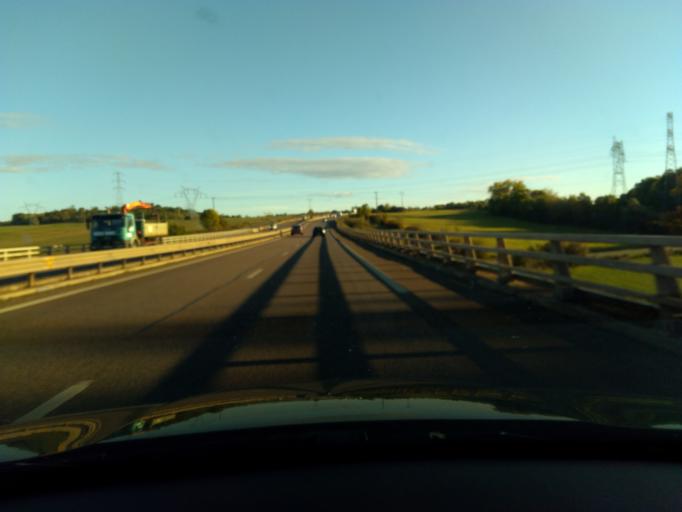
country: FR
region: Lorraine
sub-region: Departement de la Moselle
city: Saint-Julien-les-Metz
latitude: 49.1292
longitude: 6.2423
